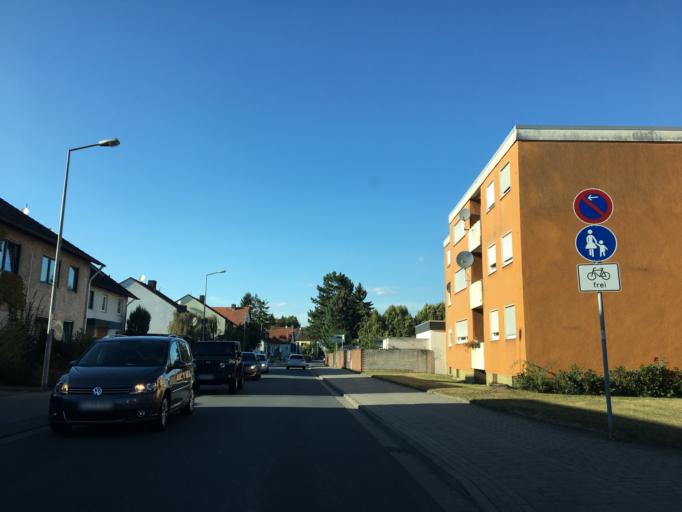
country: DE
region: Hesse
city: Morfelden-Walldorf
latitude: 49.9698
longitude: 8.5630
